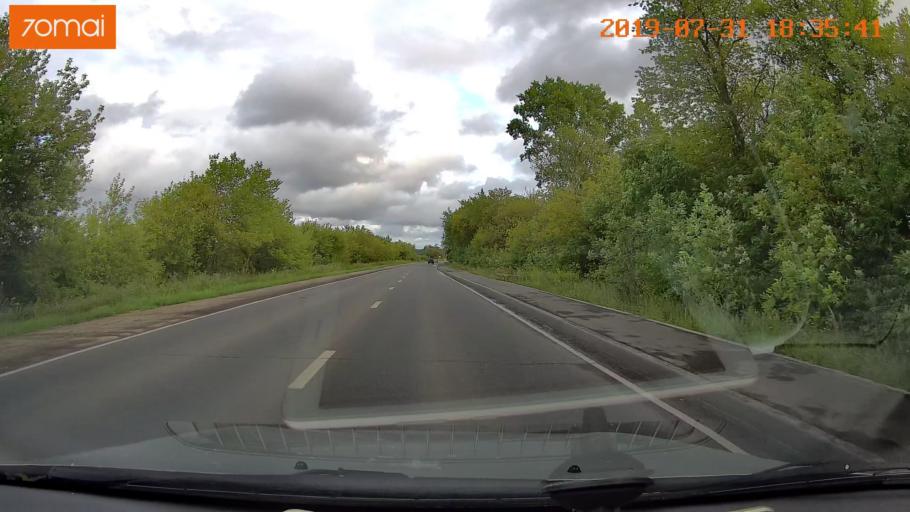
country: RU
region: Moskovskaya
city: Voskresensk
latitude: 55.2933
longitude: 38.6716
